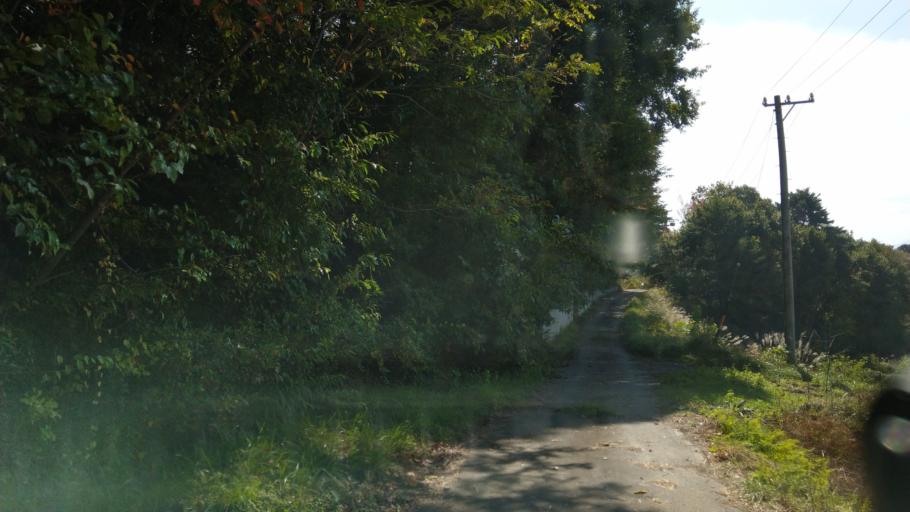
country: JP
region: Nagano
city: Komoro
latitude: 36.3571
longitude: 138.4364
